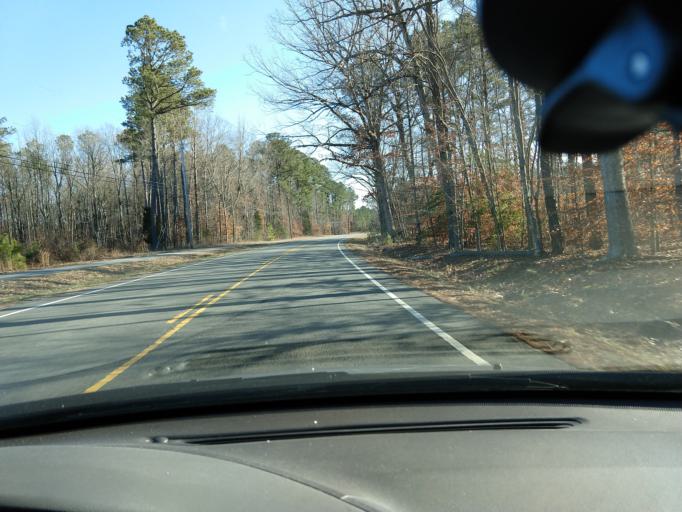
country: US
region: Virginia
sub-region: Charles City County
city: Charles City
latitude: 37.3170
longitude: -76.9691
